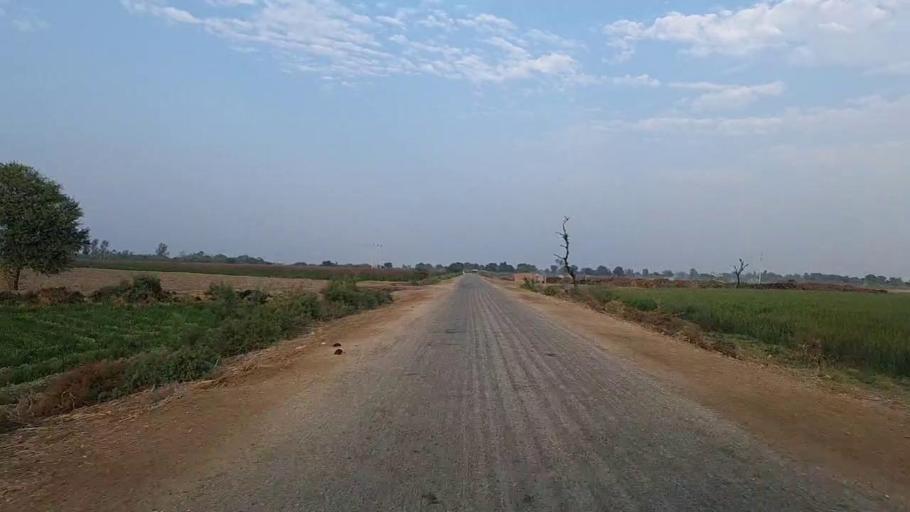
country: PK
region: Sindh
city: Pithoro
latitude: 25.4046
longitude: 69.3892
